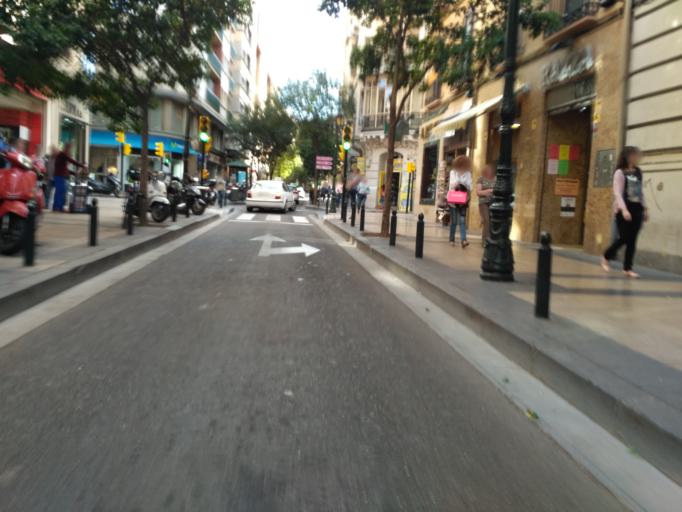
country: ES
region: Aragon
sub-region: Provincia de Zaragoza
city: Zaragoza
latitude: 41.6545
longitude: -0.8774
